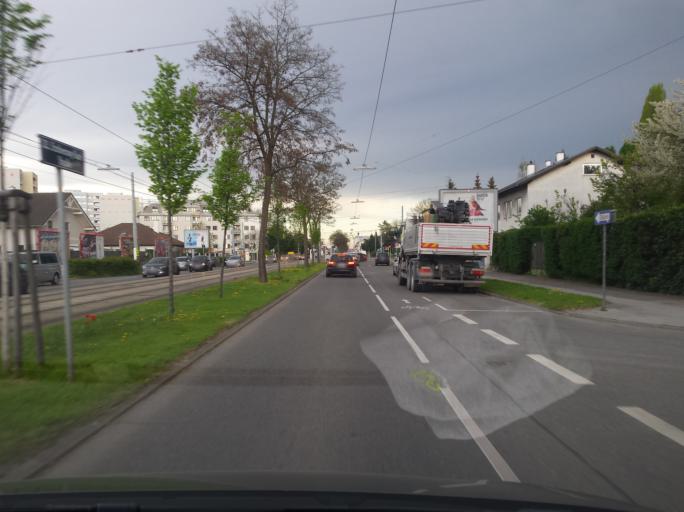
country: AT
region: Lower Austria
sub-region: Politischer Bezirk Wien-Umgebung
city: Gerasdorf bei Wien
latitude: 48.2369
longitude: 16.4360
